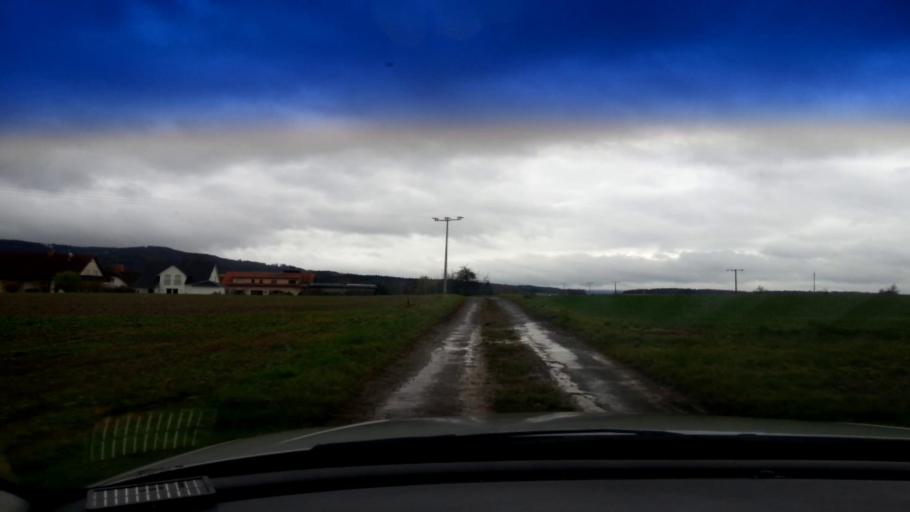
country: DE
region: Bavaria
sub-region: Upper Franconia
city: Ebensfeld
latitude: 50.0359
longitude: 10.9968
